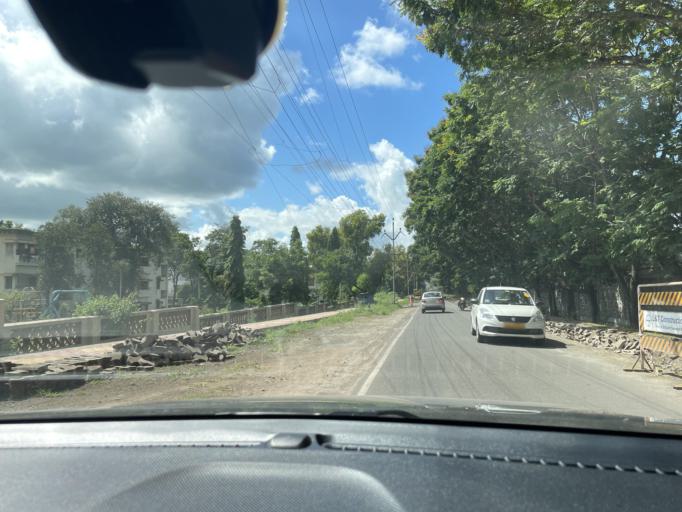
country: IN
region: Maharashtra
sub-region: Pune Division
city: Shivaji Nagar
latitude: 18.5264
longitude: 73.7805
